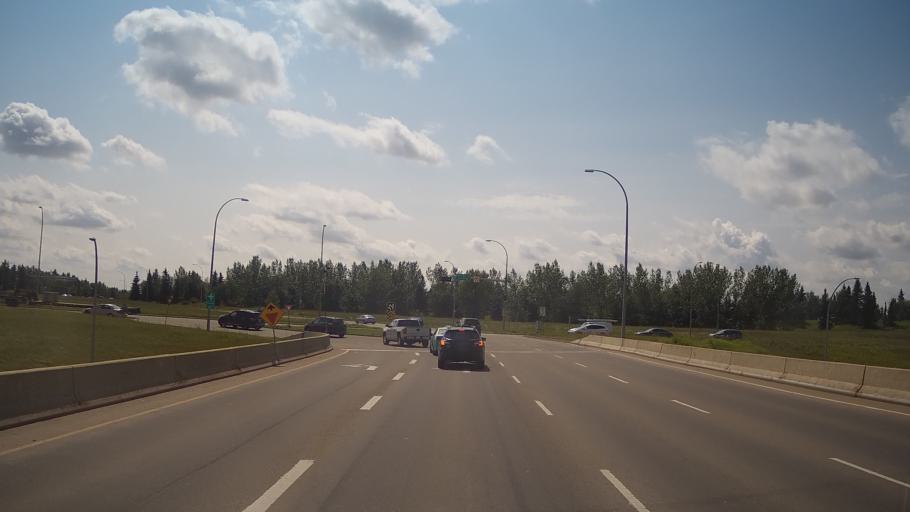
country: CA
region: Alberta
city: St. Albert
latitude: 53.5122
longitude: -113.6161
